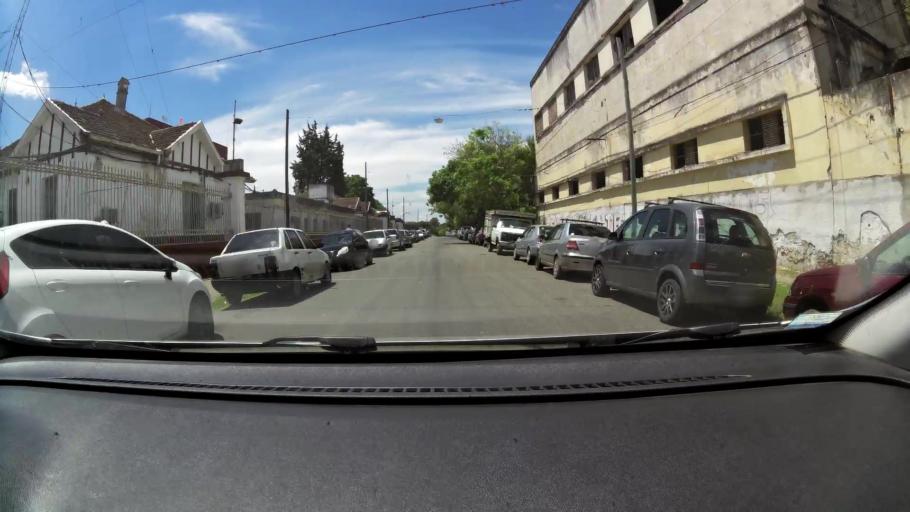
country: AR
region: Santa Fe
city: Gobernador Galvez
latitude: -32.9963
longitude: -60.6229
